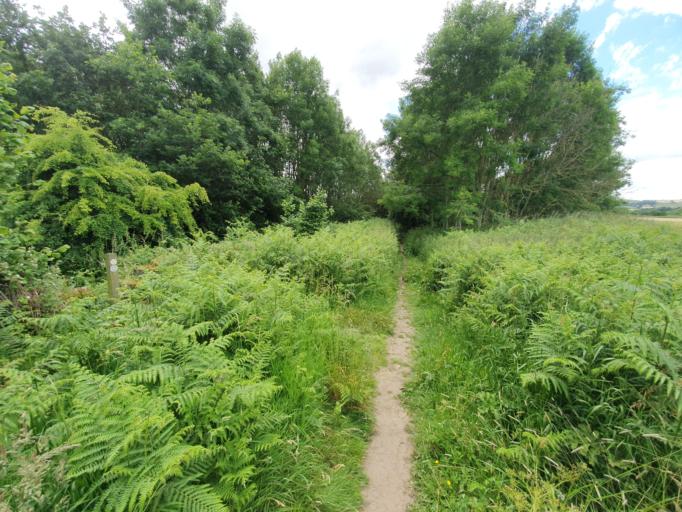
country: GB
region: England
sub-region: Bradford
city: Menston
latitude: 53.8639
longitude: -1.7407
